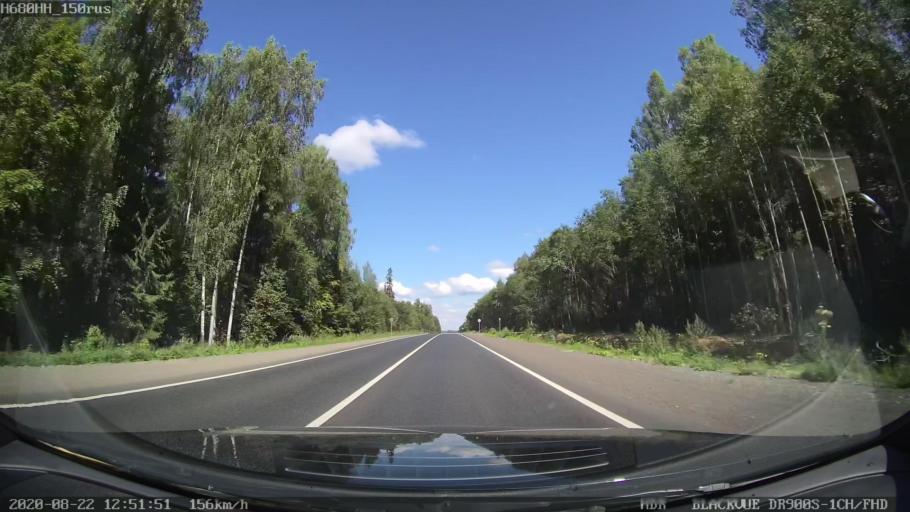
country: RU
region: Tverskaya
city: Rameshki
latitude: 57.4916
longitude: 36.2517
